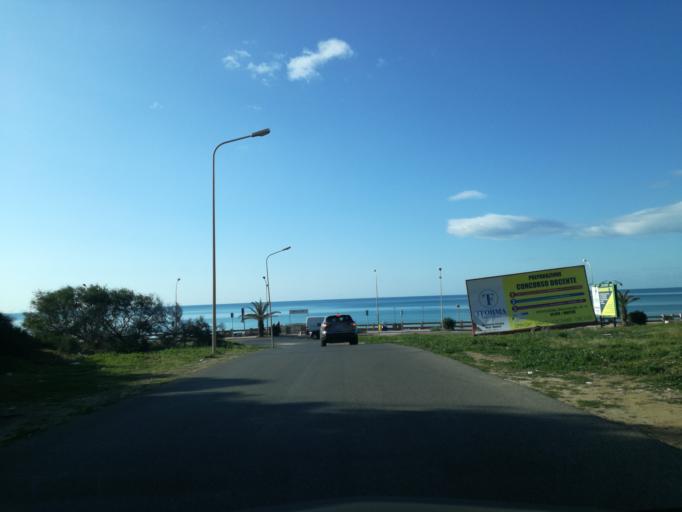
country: IT
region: Sicily
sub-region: Provincia di Caltanissetta
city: Gela
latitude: 37.0737
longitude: 14.2183
